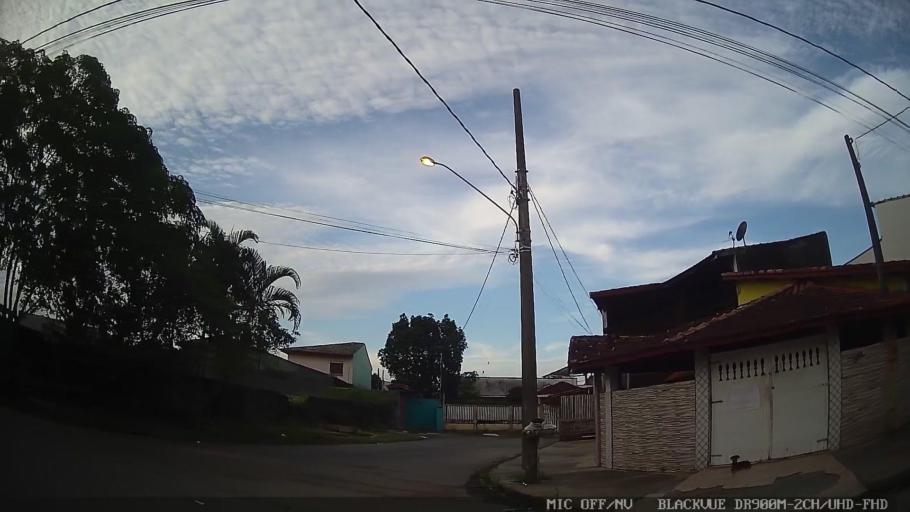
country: BR
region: Sao Paulo
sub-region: Itanhaem
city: Itanhaem
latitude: -24.1664
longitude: -46.7747
